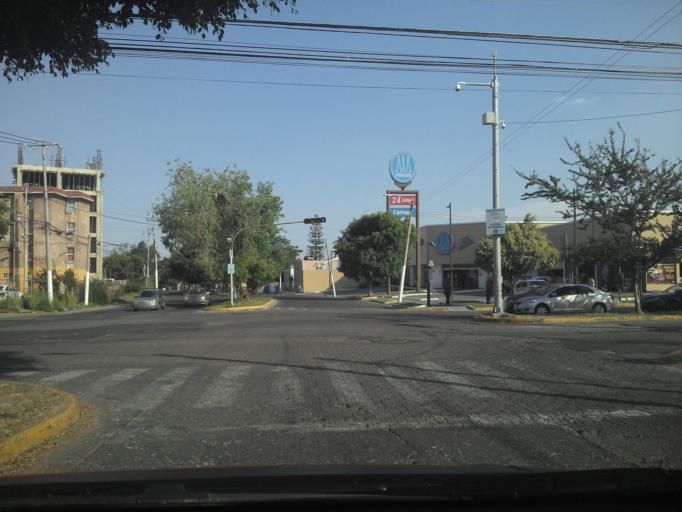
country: MX
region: Jalisco
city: Guadalajara
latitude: 20.6524
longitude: -103.4417
